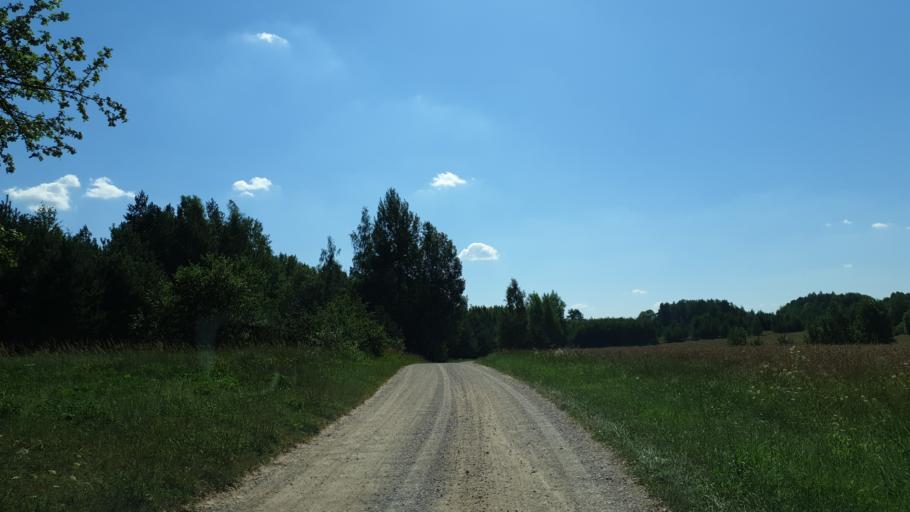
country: LT
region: Vilnius County
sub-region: Vilniaus Rajonas
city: Vievis
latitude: 54.9036
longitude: 24.8790
